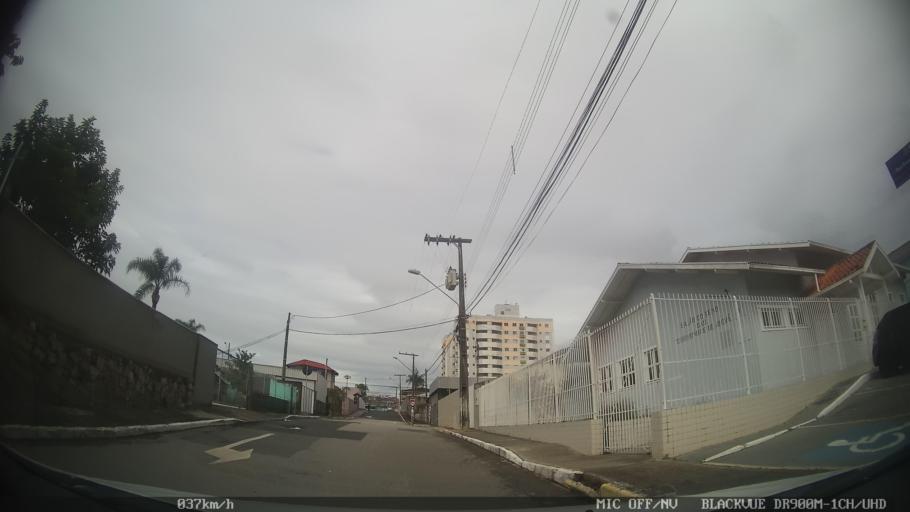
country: BR
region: Santa Catarina
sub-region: Sao Jose
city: Campinas
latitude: -27.5619
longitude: -48.6353
